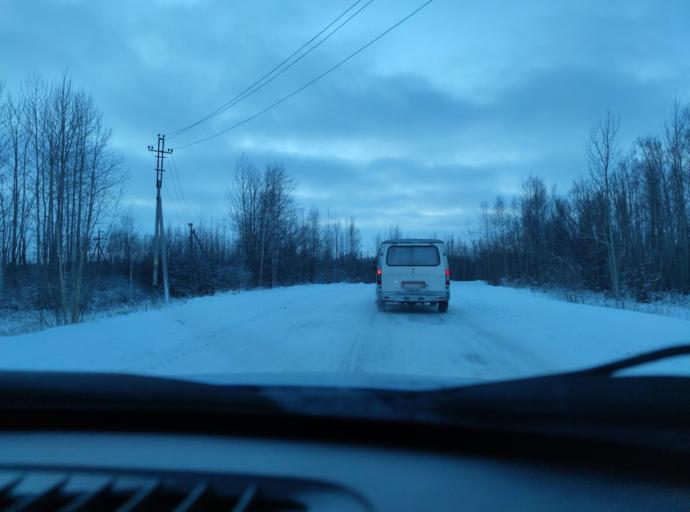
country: RU
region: Khanty-Mansiyskiy Avtonomnyy Okrug
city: Langepas
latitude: 61.1841
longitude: 75.1634
